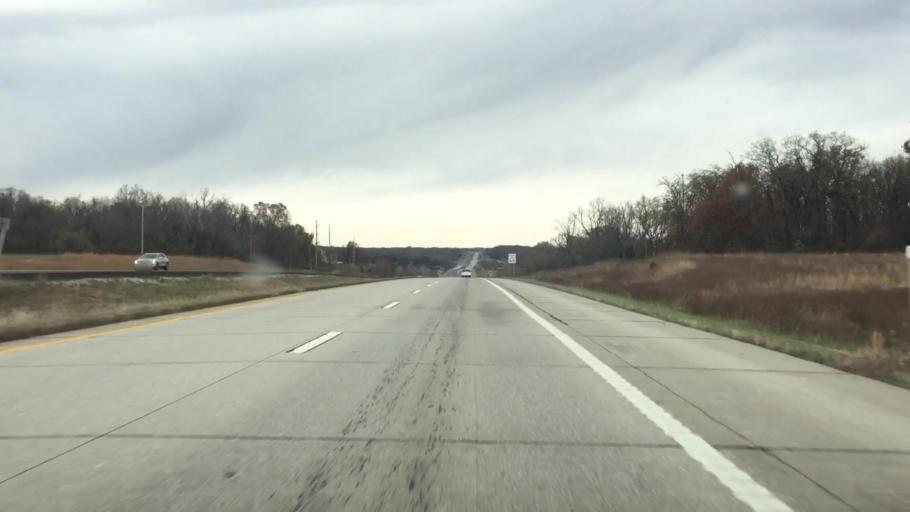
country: US
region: Missouri
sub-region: Saint Clair County
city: Osceola
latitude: 38.0470
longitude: -93.6849
